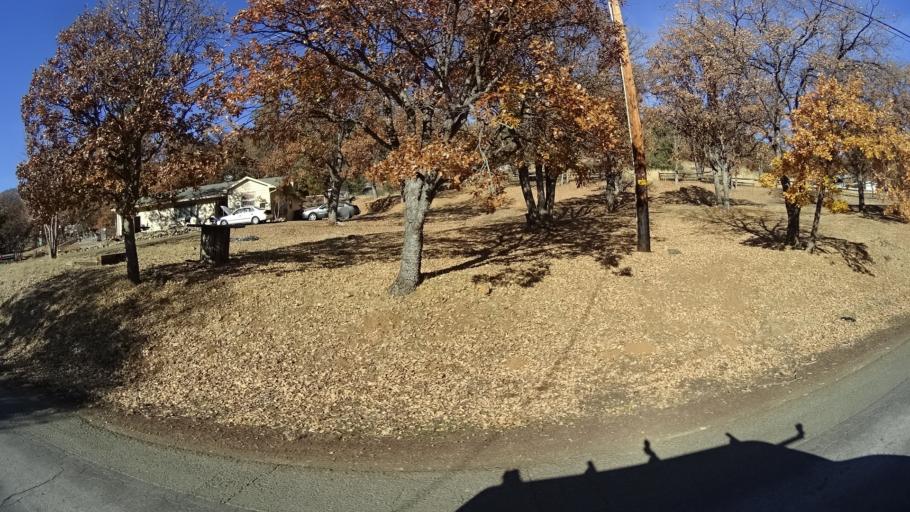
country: US
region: California
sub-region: Siskiyou County
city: Yreka
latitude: 41.7173
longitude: -122.6682
